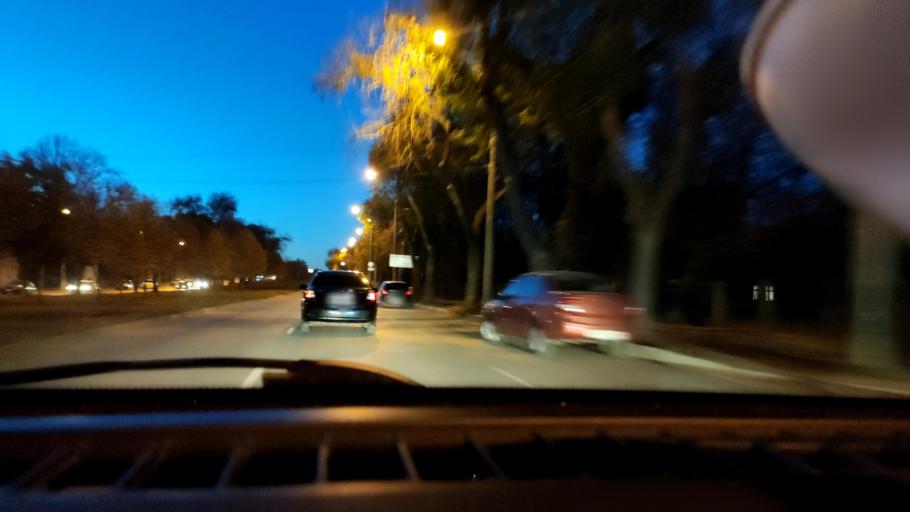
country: RU
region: Samara
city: Samara
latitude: 53.2195
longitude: 50.2402
